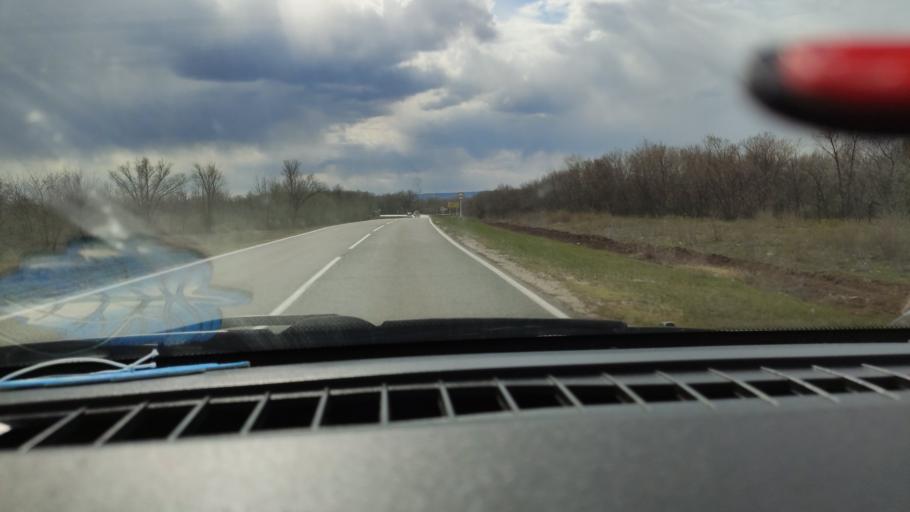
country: RU
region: Saratov
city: Privolzhskiy
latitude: 51.2783
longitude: 45.9518
